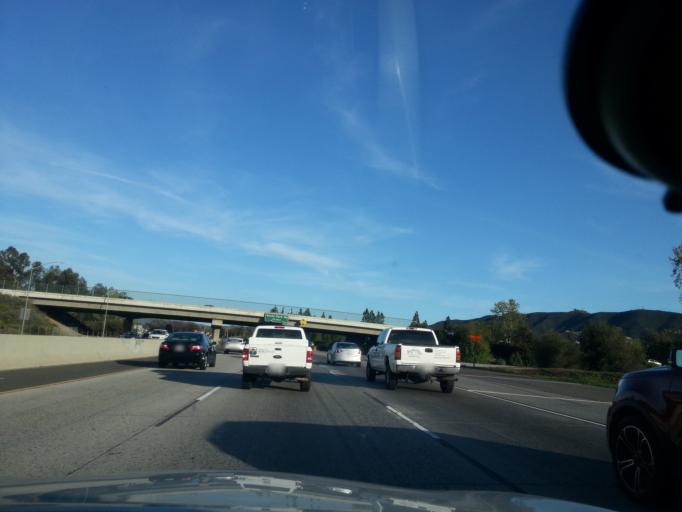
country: US
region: California
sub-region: Ventura County
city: Casa Conejo
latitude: 34.1847
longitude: -118.9273
